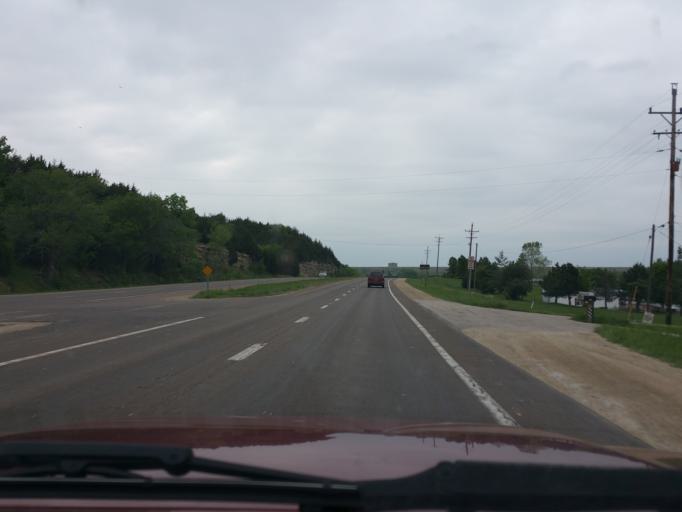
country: US
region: Kansas
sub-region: Riley County
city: Manhattan
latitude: 39.2397
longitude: -96.5913
